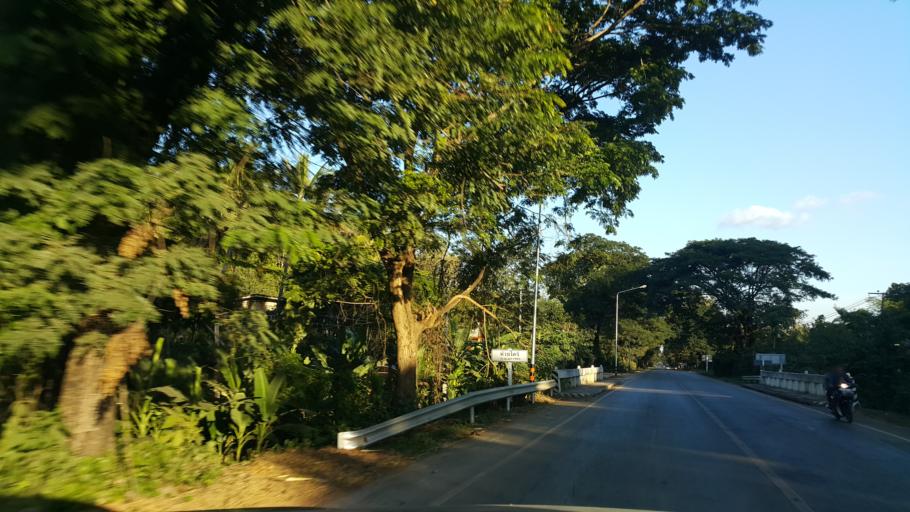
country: TH
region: Sukhothai
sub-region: Amphoe Si Satchanalai
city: Si Satchanalai
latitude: 17.5519
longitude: 99.8803
